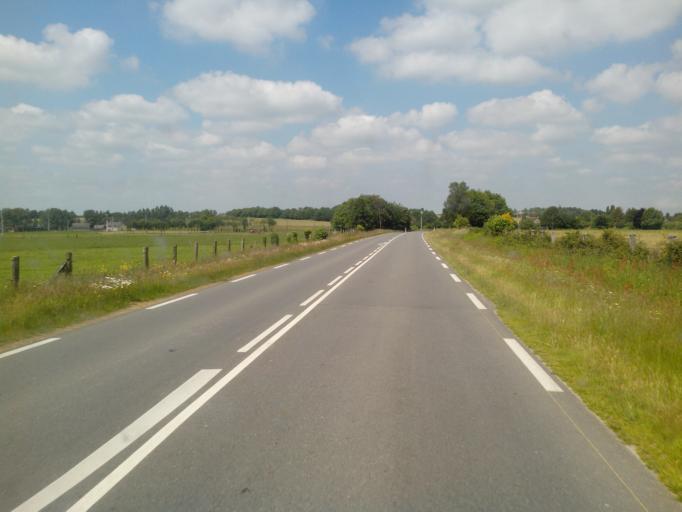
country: FR
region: Brittany
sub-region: Departement d'Ille-et-Vilaine
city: Saint-Germain-en-Cogles
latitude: 48.3934
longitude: -1.2885
